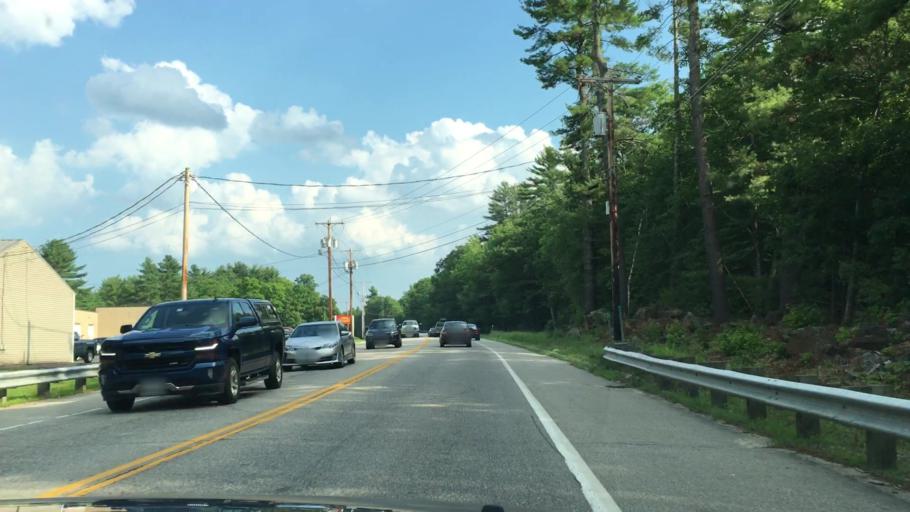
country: US
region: New Hampshire
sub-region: Strafford County
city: Farmington
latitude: 43.3614
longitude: -71.0357
